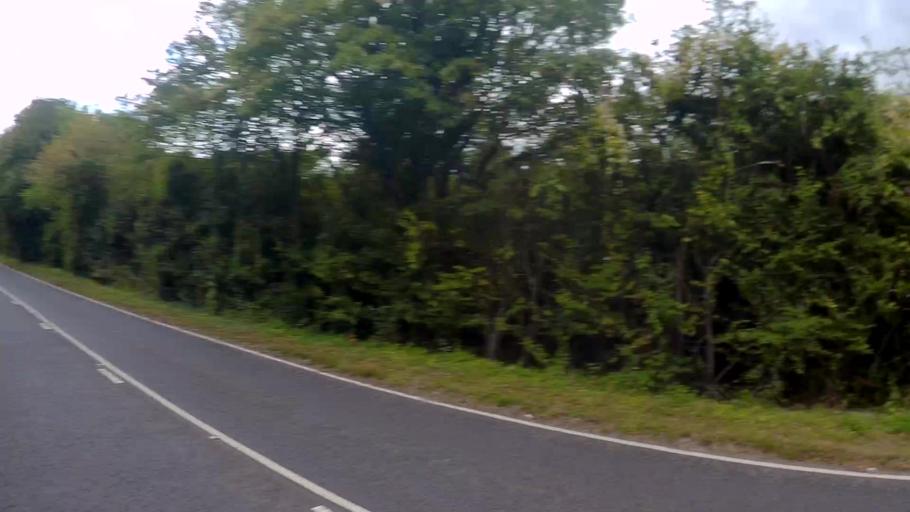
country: GB
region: England
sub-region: Hampshire
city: Overton
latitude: 51.1897
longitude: -1.2619
